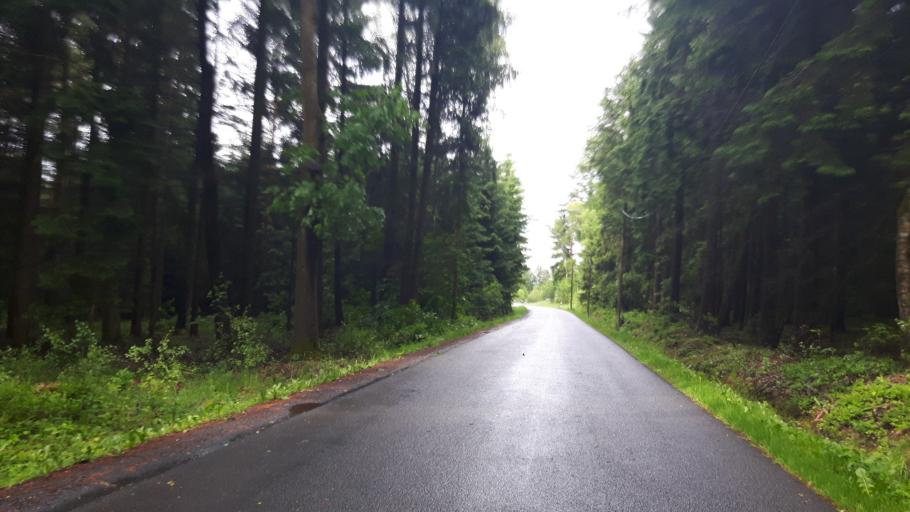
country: DE
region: Thuringia
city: Bockstadt
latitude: 50.4095
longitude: 10.8975
